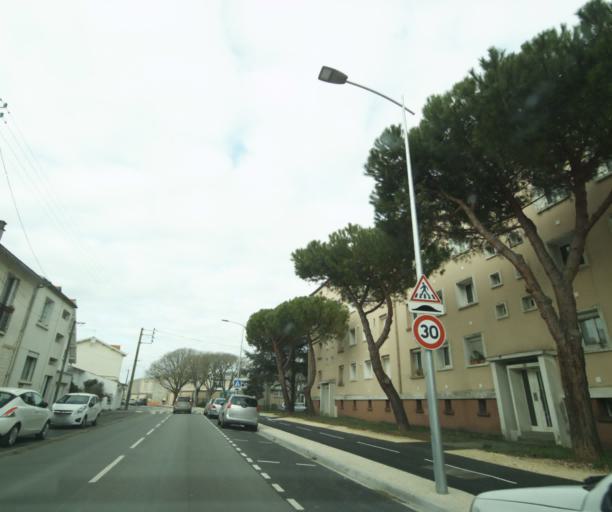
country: FR
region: Poitou-Charentes
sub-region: Departement de la Charente-Maritime
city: La Rochelle
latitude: 46.1691
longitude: -1.1637
